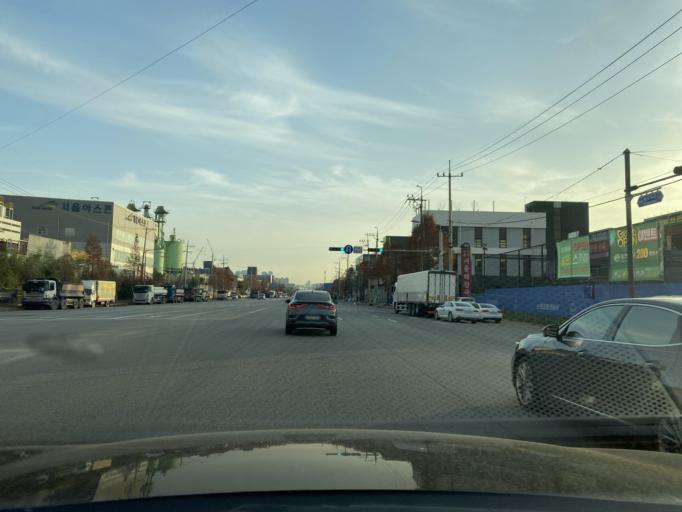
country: KR
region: Incheon
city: Incheon
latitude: 37.5038
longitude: 126.6616
